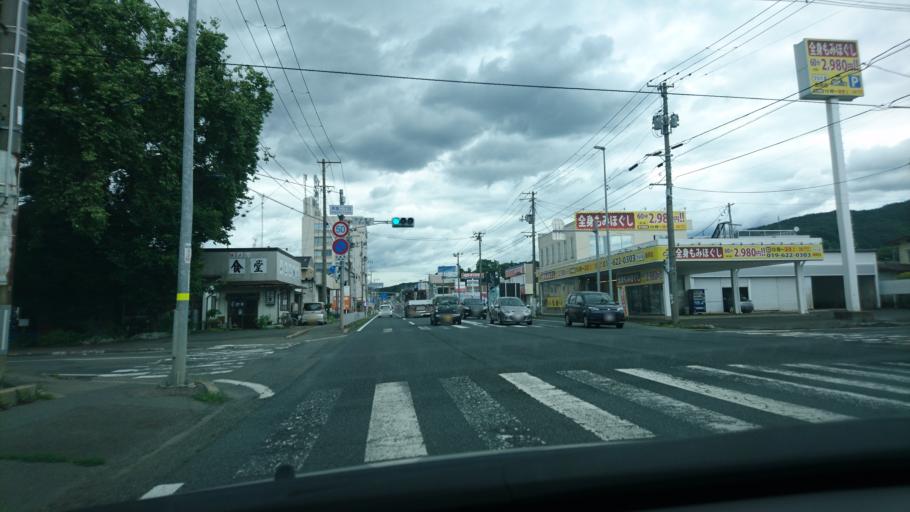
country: JP
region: Iwate
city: Morioka-shi
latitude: 39.6924
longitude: 141.1663
